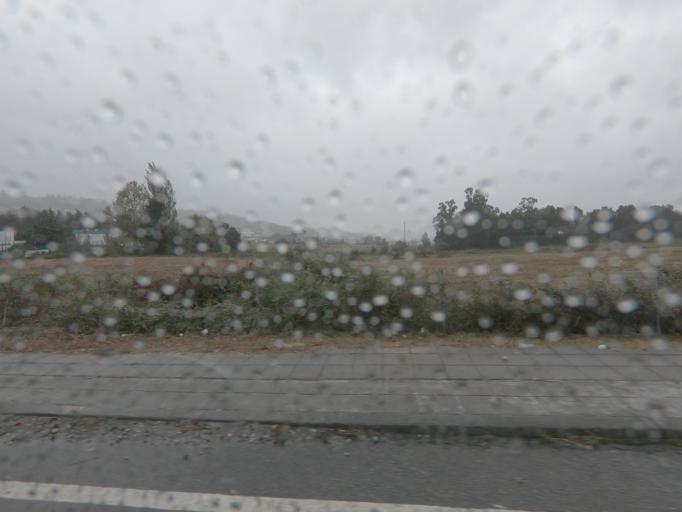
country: PT
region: Porto
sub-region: Penafiel
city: Penafiel
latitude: 41.1918
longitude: -8.3054
